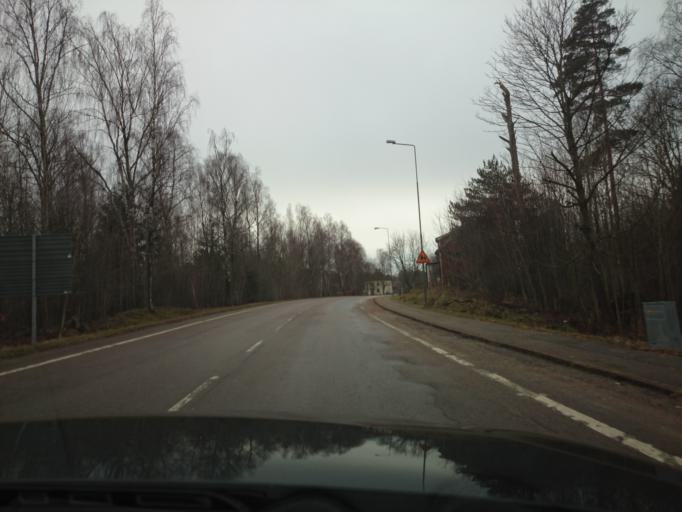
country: SE
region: Halland
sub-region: Hylte Kommun
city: Torup
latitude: 56.9640
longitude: 13.1463
